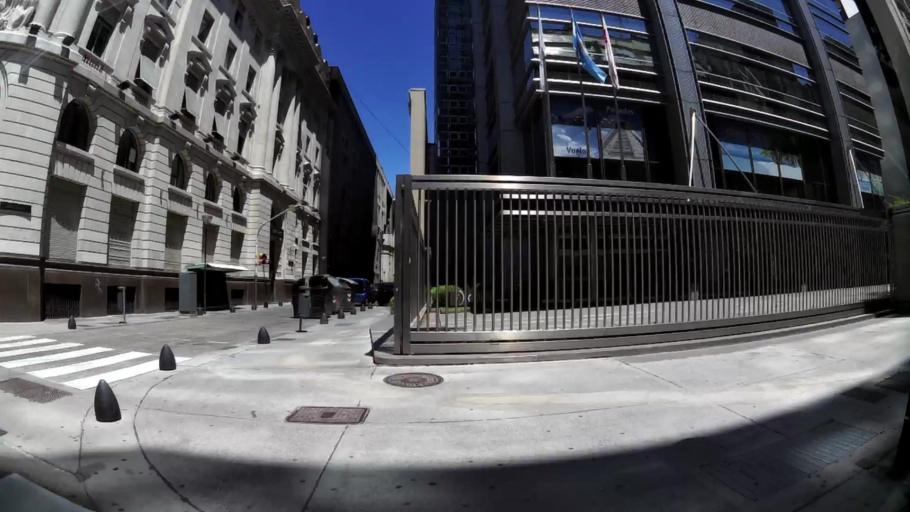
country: AR
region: Buenos Aires F.D.
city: Buenos Aires
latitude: -34.6055
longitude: -58.3726
